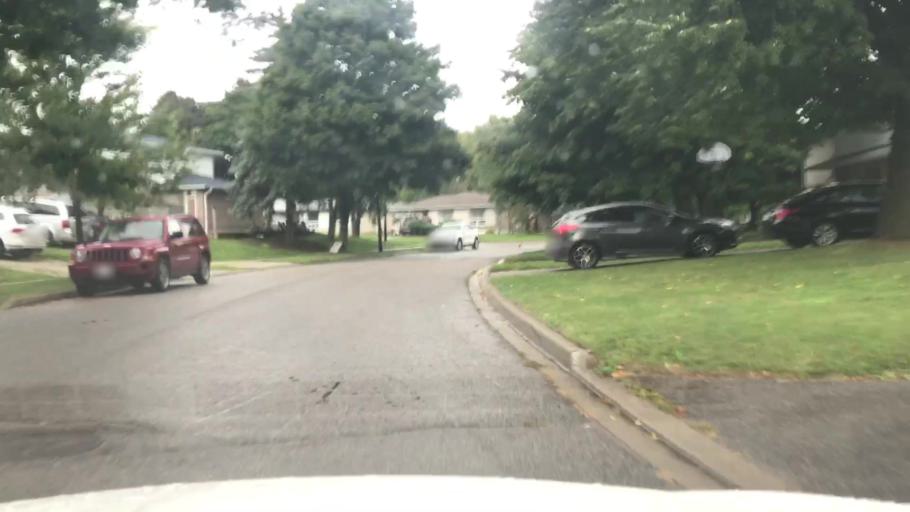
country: CA
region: Ontario
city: Newmarket
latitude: 44.0452
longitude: -79.4638
